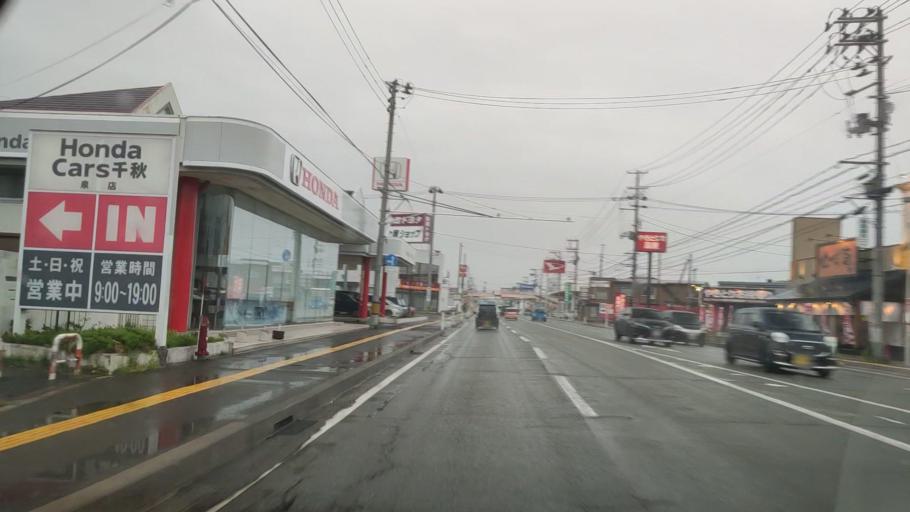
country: JP
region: Akita
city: Akita Shi
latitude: 39.7335
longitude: 140.1008
